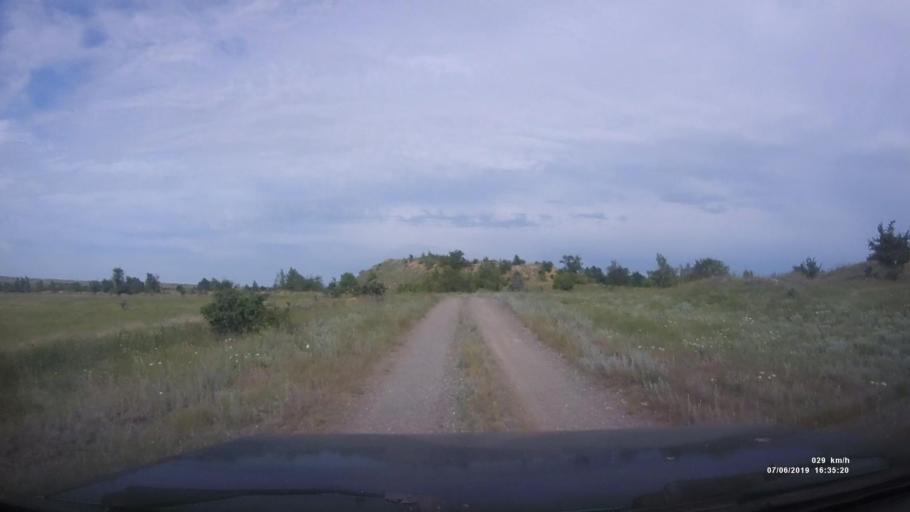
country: RU
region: Rostov
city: Staraya Stanitsa
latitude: 48.2515
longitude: 40.3475
